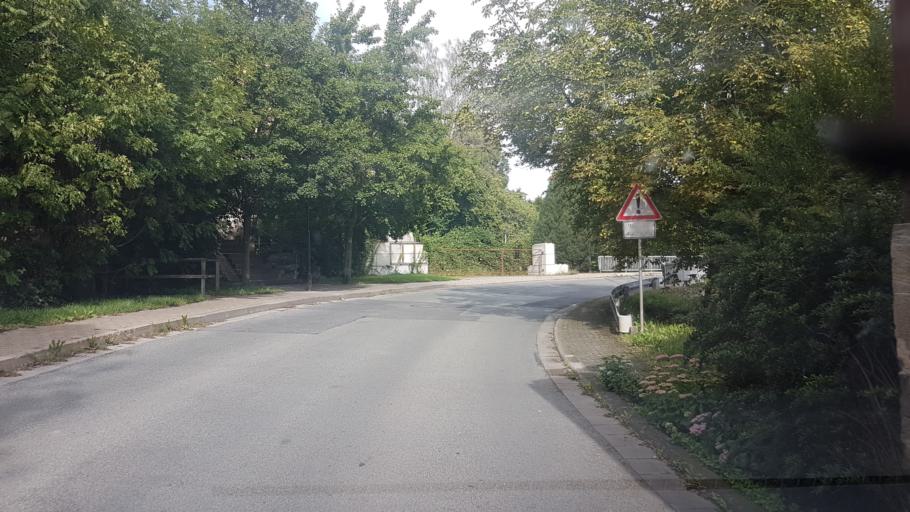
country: DE
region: Bavaria
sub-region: Upper Franconia
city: Grossheirath
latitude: 50.1977
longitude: 10.9528
